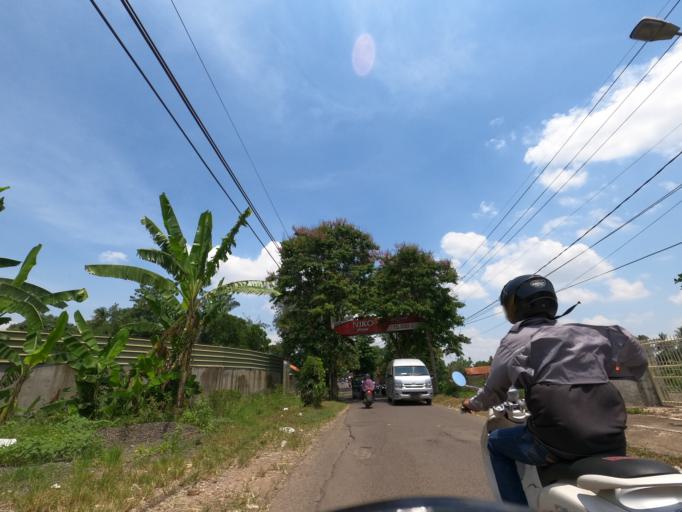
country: ID
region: West Java
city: Pamanukan
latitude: -6.5392
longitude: 107.7691
